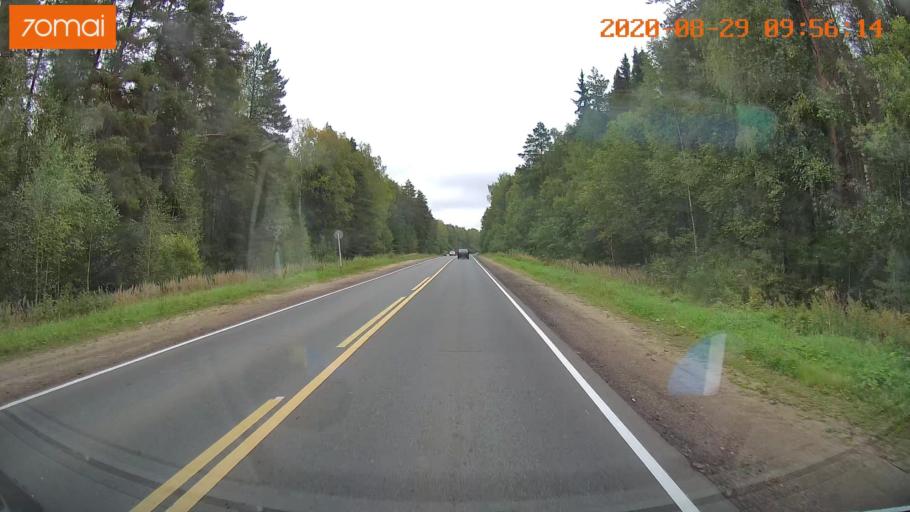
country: RU
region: Ivanovo
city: Zarechnyy
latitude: 57.4210
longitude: 42.2839
